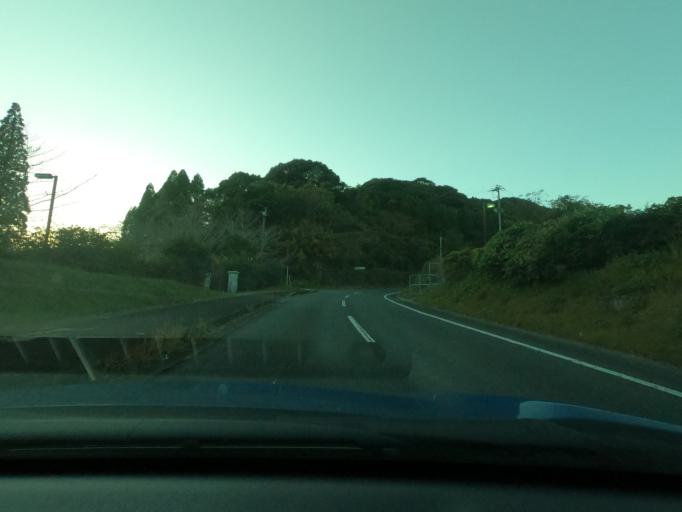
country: JP
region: Kagoshima
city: Satsumasendai
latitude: 31.8102
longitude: 130.4845
